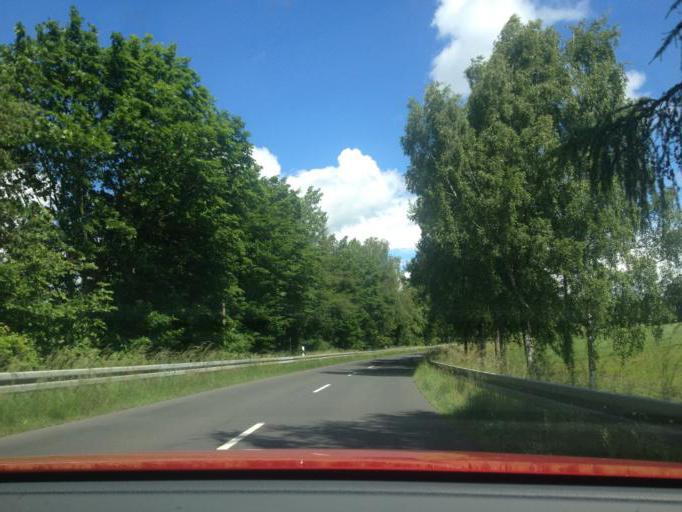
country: DE
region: Bavaria
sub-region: Upper Palatinate
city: Pechbrunn
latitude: 49.9798
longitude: 12.1737
